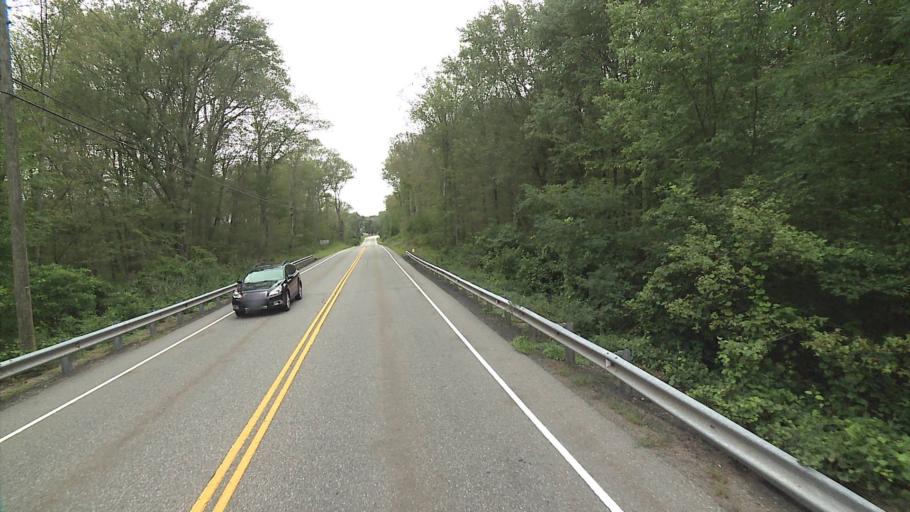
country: US
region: Connecticut
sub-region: Hartford County
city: Terramuggus
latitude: 41.7166
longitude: -72.4348
